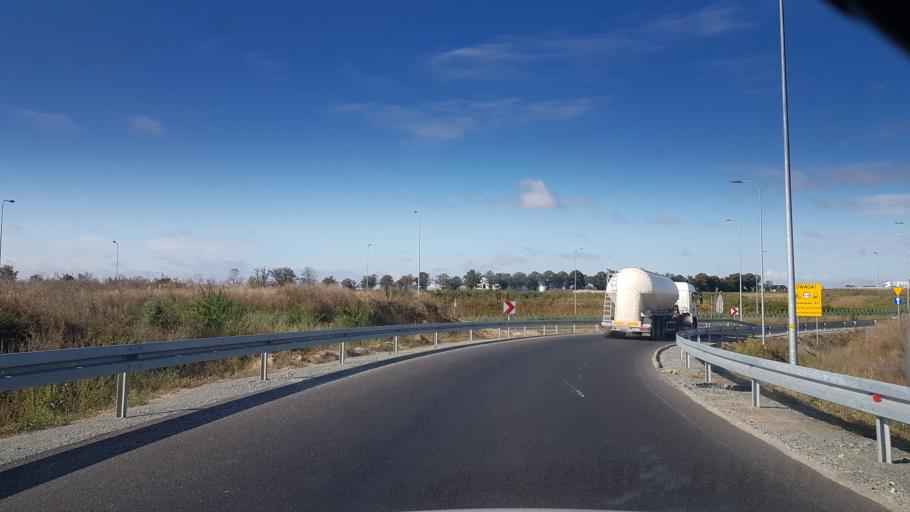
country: PL
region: Greater Poland Voivodeship
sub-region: Powiat poznanski
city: Steszew
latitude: 52.2251
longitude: 16.6943
